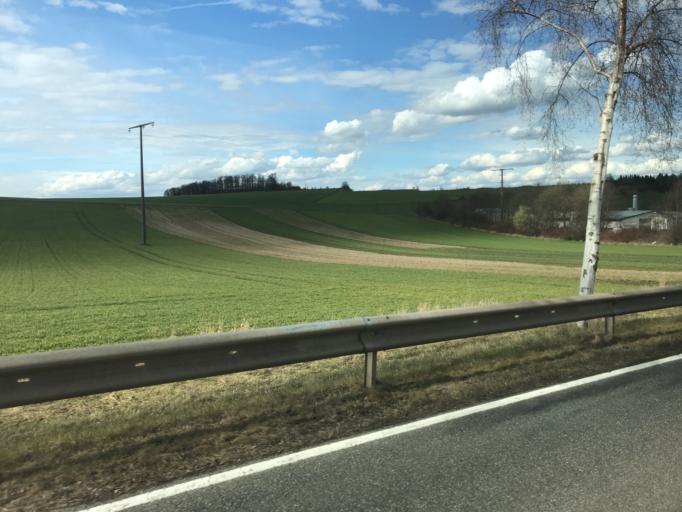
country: DE
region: Rheinland-Pfalz
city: Wassenach
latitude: 50.4381
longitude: 7.2778
